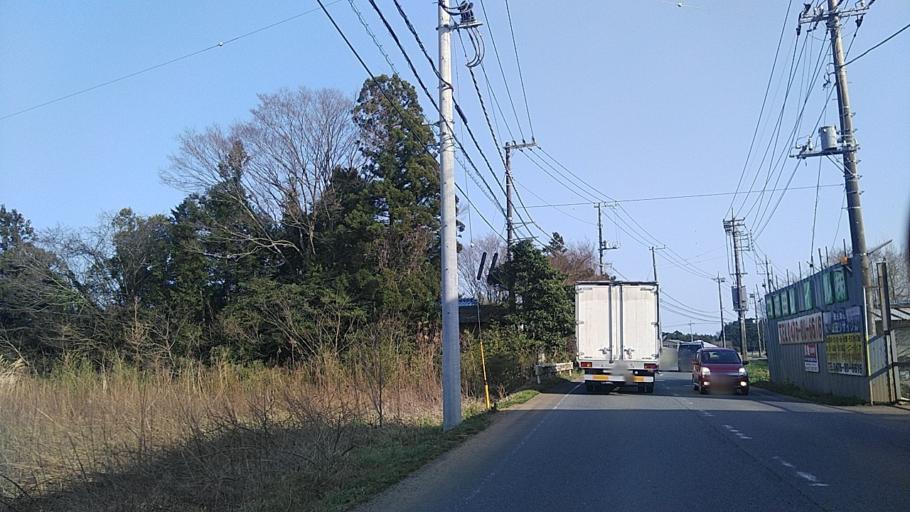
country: JP
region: Chiba
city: Narita
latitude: 35.8429
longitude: 140.3912
